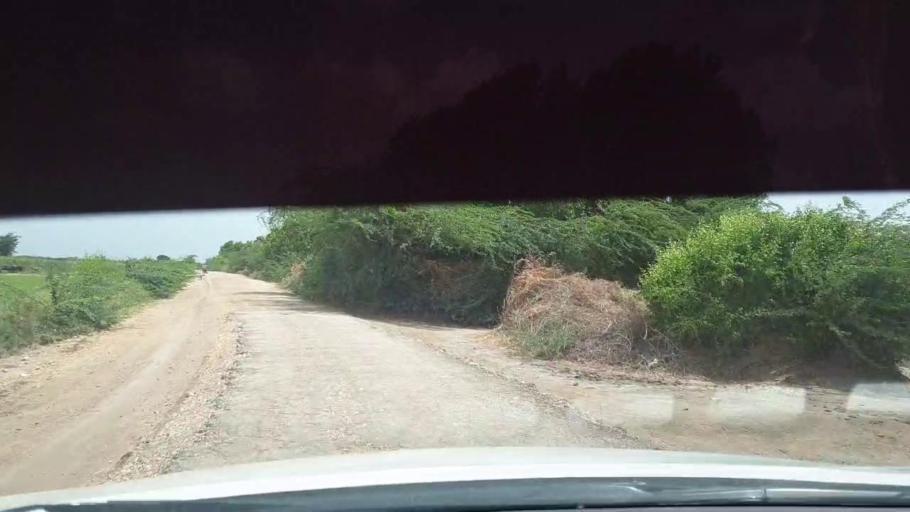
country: PK
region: Sindh
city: Kadhan
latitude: 24.4943
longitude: 68.9828
